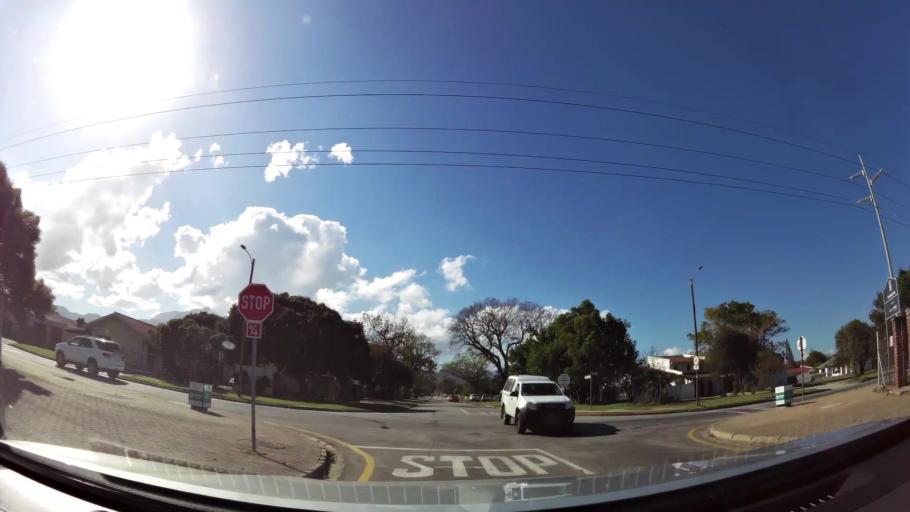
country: ZA
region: Western Cape
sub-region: Eden District Municipality
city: George
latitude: -33.9736
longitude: 22.4495
